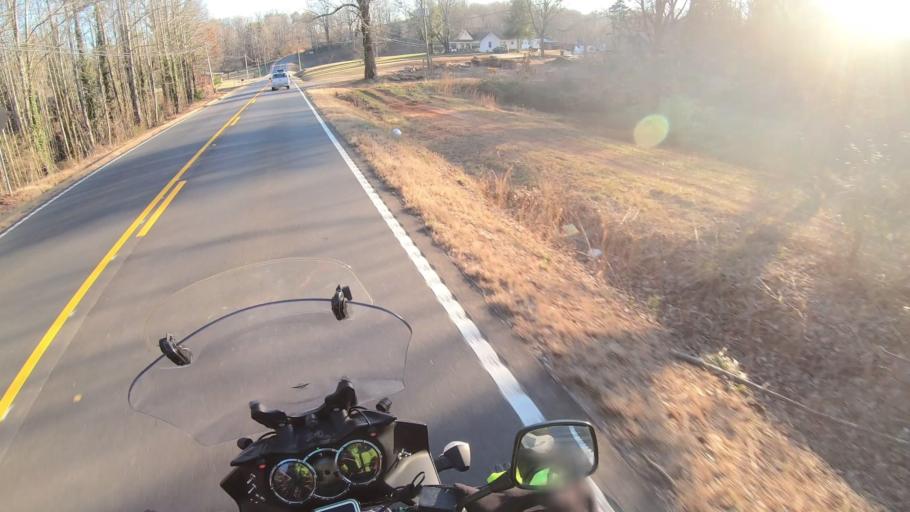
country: US
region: Georgia
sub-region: Lumpkin County
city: Dahlonega
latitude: 34.5762
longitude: -83.9702
